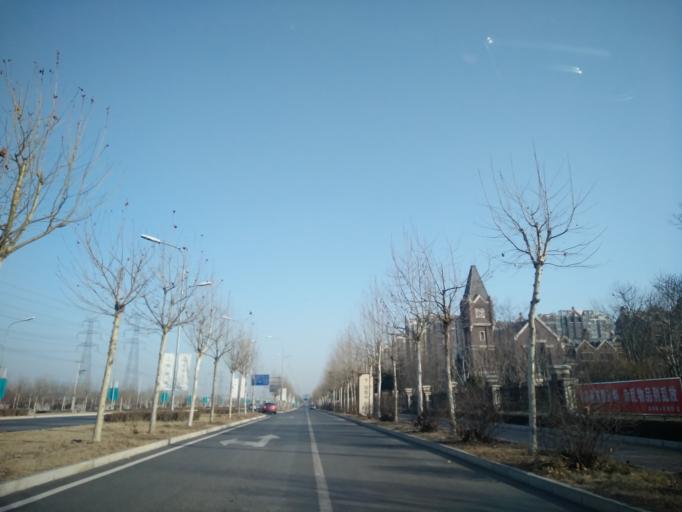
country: CN
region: Beijing
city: Yinghai
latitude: 39.7551
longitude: 116.4759
